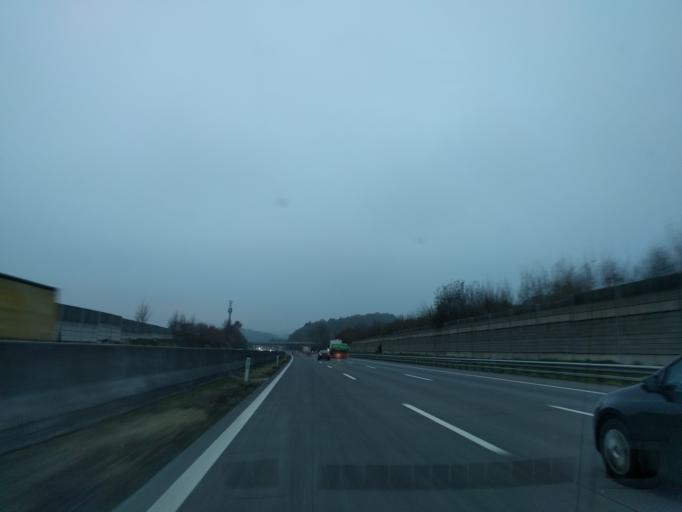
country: AT
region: Lower Austria
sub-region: Politischer Bezirk Melk
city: Blindenmarkt
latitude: 48.1337
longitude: 14.9902
